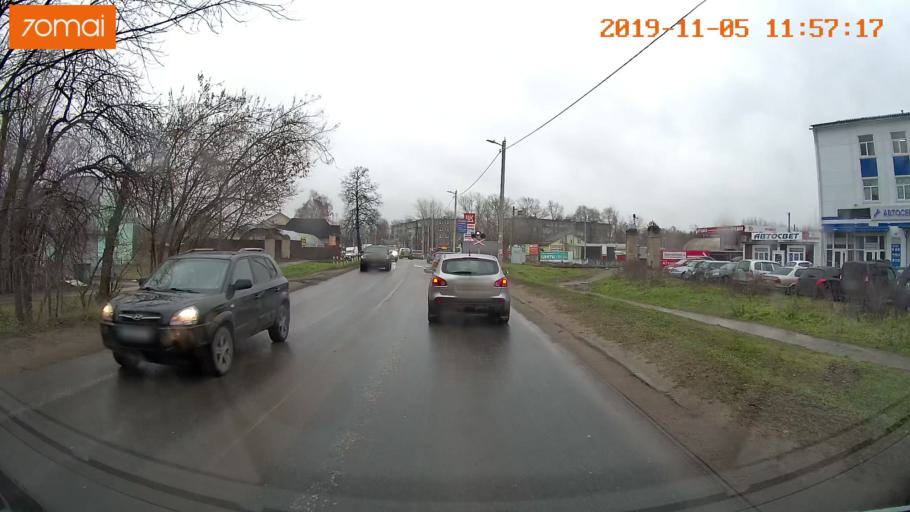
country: RU
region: Ivanovo
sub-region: Gorod Ivanovo
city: Ivanovo
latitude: 56.9835
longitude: 41.0341
